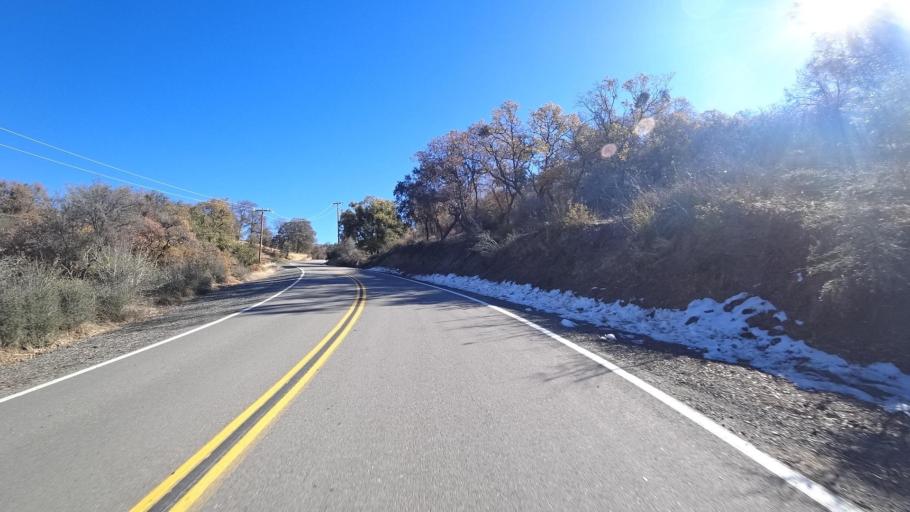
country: US
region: California
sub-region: Kern County
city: Alta Sierra
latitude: 35.7381
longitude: -118.6308
